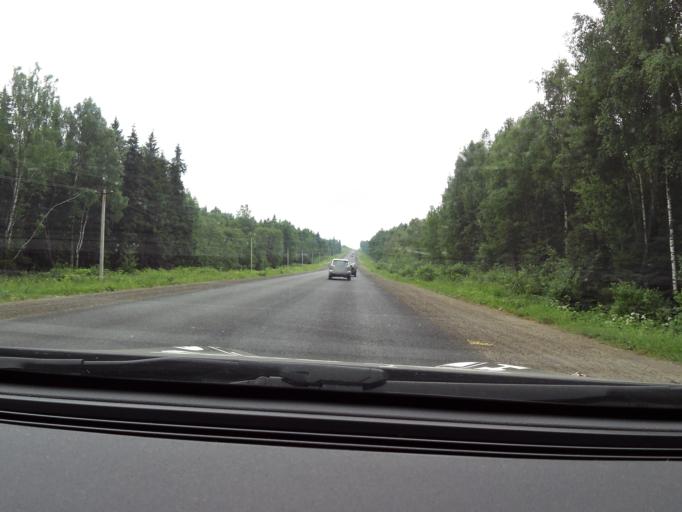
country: RU
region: Perm
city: Bershet'
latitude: 57.7631
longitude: 56.3590
